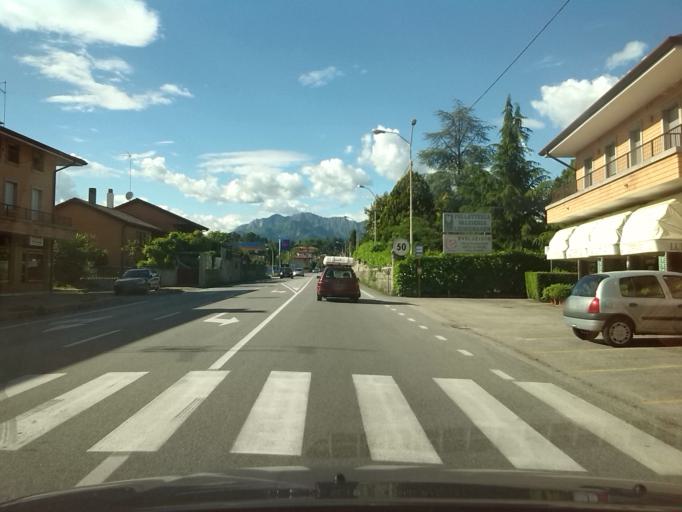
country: IT
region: Friuli Venezia Giulia
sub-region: Provincia di Udine
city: Tricesimo
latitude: 46.1525
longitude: 13.2192
